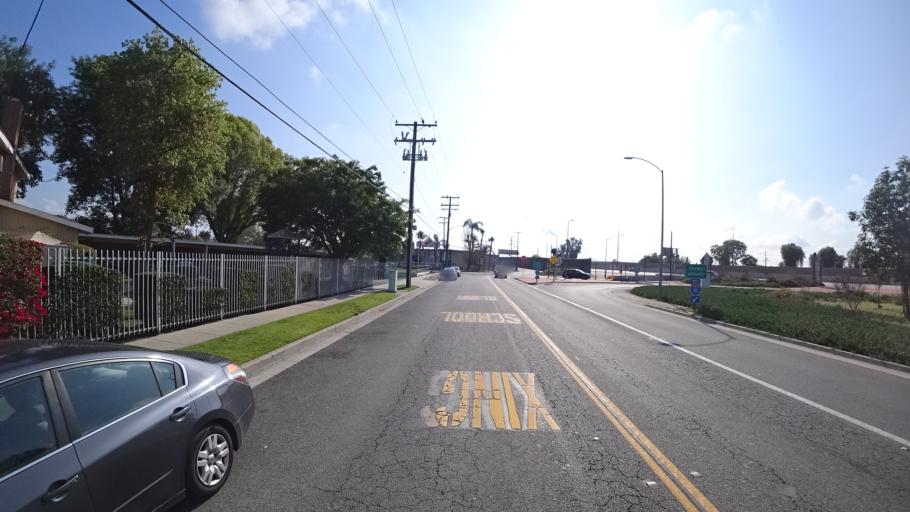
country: US
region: California
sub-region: Los Angeles County
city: West Puente Valley
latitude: 34.0698
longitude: -117.9719
